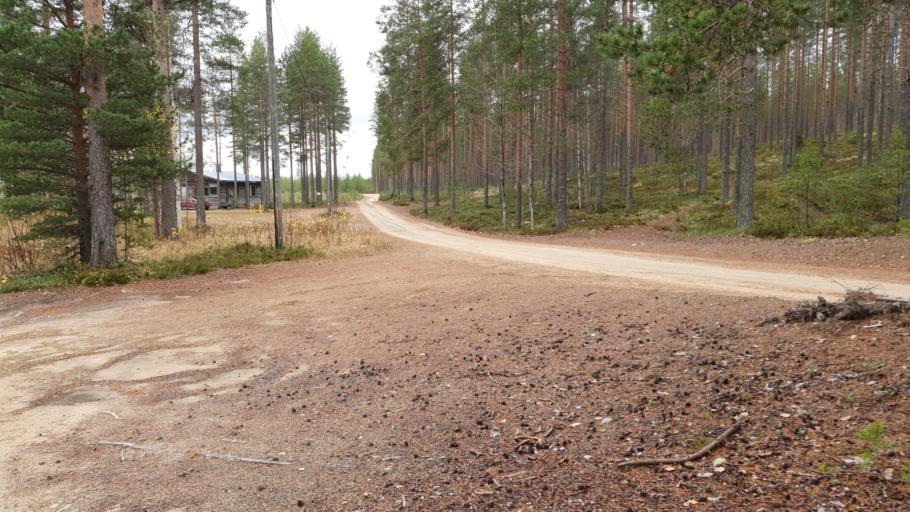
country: FI
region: Kainuu
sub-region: Kehys-Kainuu
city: Kuhmo
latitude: 64.1515
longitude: 29.3890
